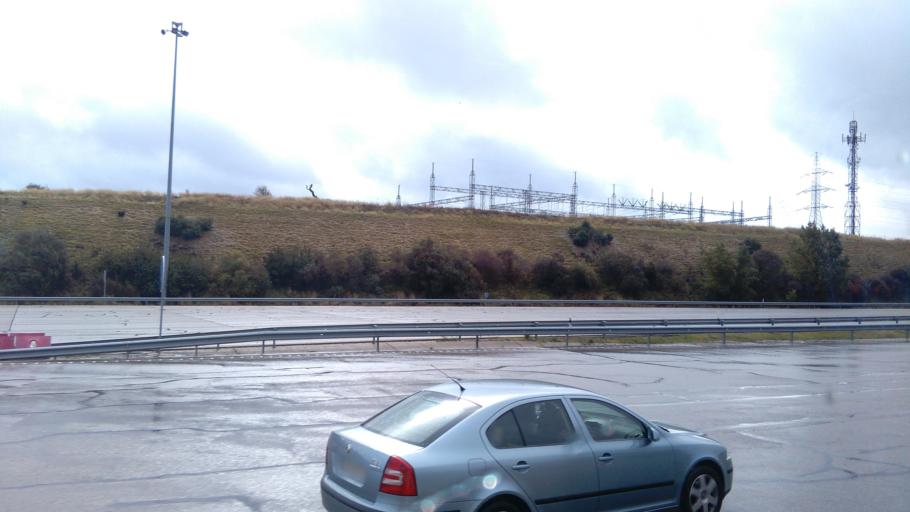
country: ES
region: Madrid
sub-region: Provincia de Madrid
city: Leganes
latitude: 40.3493
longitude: -3.7832
